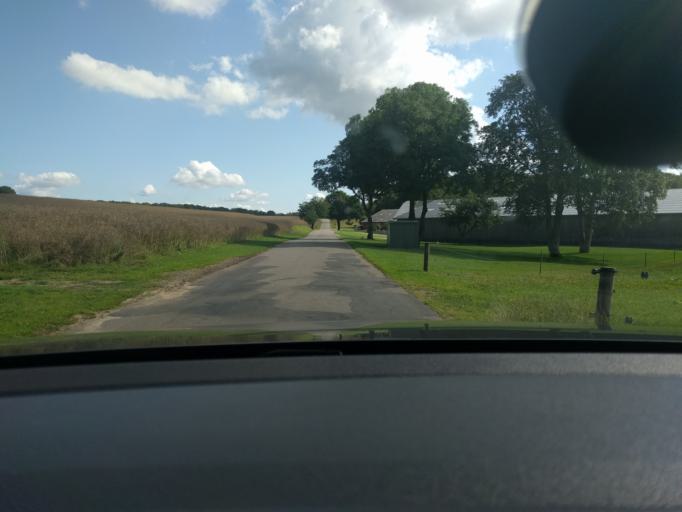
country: DK
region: Central Jutland
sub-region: Viborg Kommune
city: Viborg
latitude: 56.4899
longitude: 9.2770
